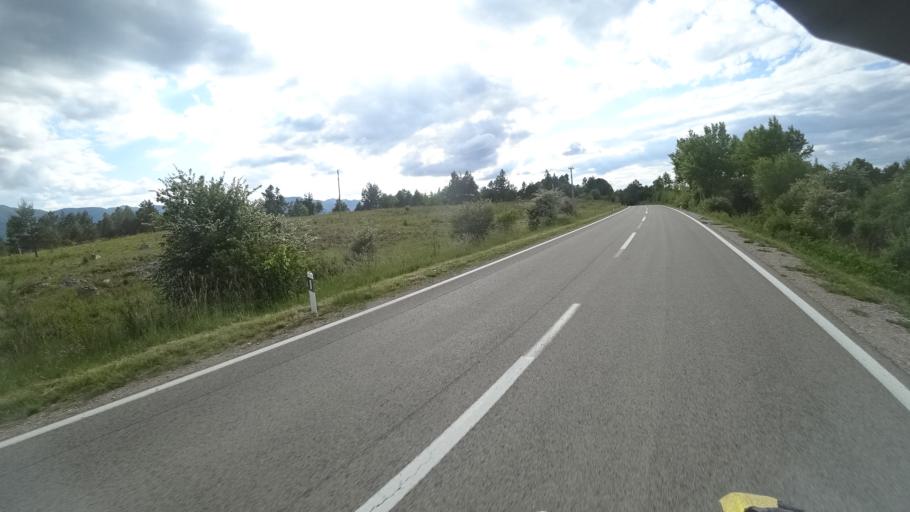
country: HR
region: Licko-Senjska
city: Gospic
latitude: 44.5060
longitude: 15.4443
